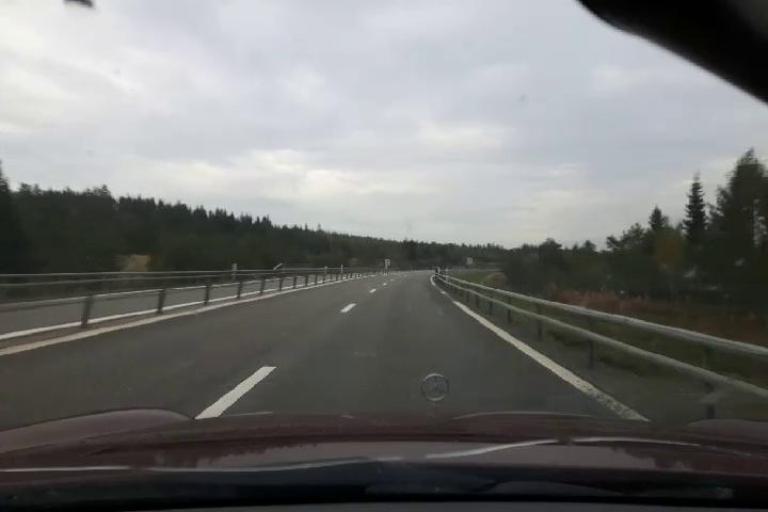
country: SE
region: Vaesternorrland
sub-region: Haernoesands Kommun
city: Haernoesand
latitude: 62.7206
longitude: 17.9178
